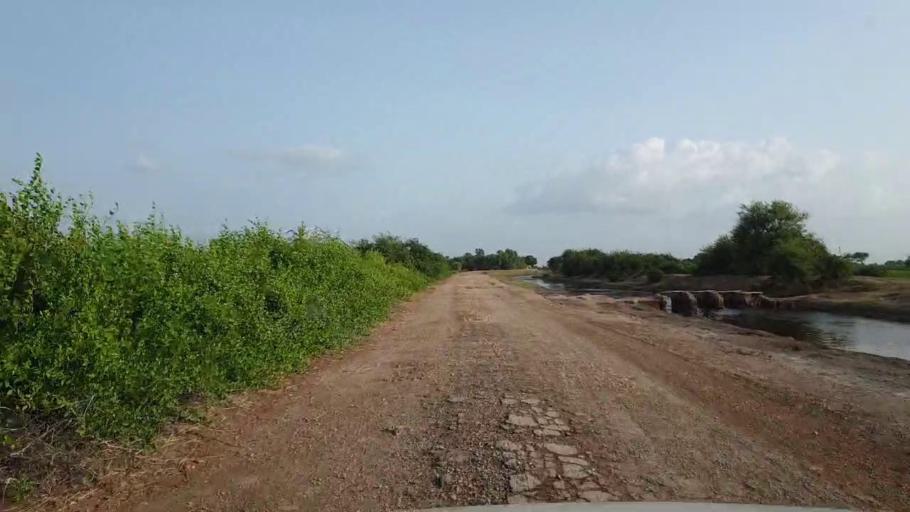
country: PK
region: Sindh
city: Kario
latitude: 24.8394
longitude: 68.6523
